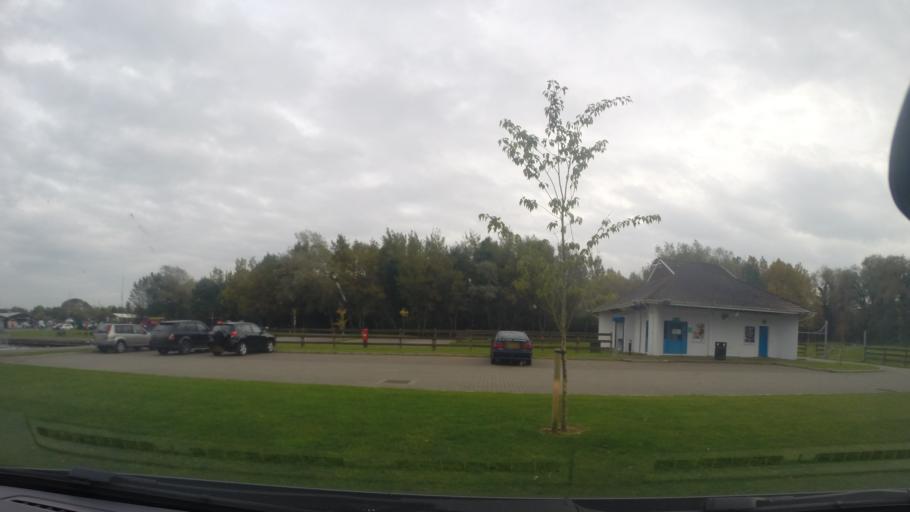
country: GB
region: Northern Ireland
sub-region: Craigavon District
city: Craigavon
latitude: 54.4892
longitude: -6.3661
